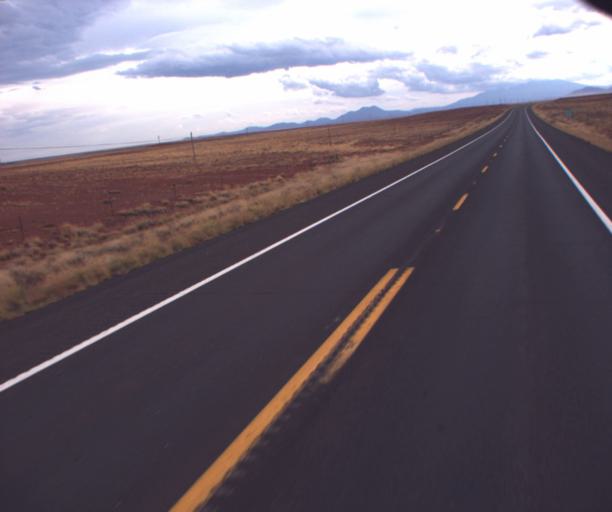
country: US
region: Arizona
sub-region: Coconino County
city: Tuba City
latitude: 35.7264
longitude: -111.4824
